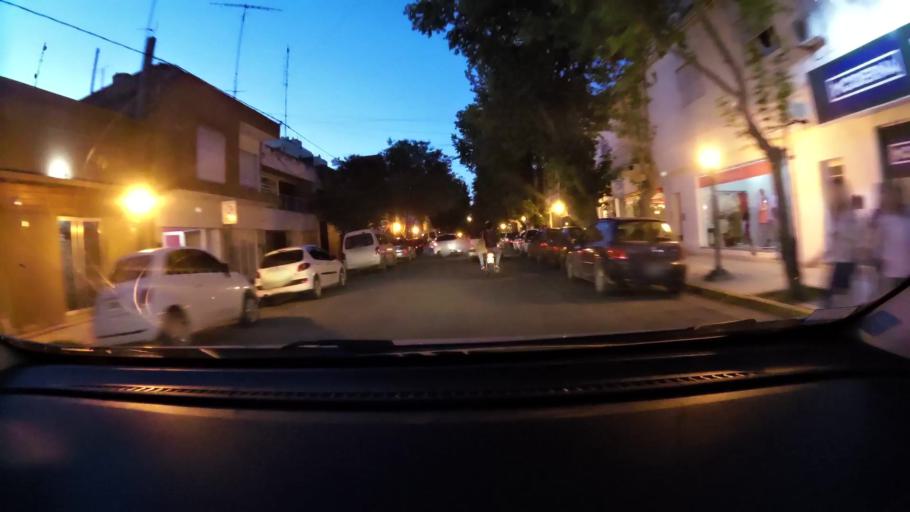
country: AR
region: Cordoba
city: Villa Maria
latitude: -32.4098
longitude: -63.2413
